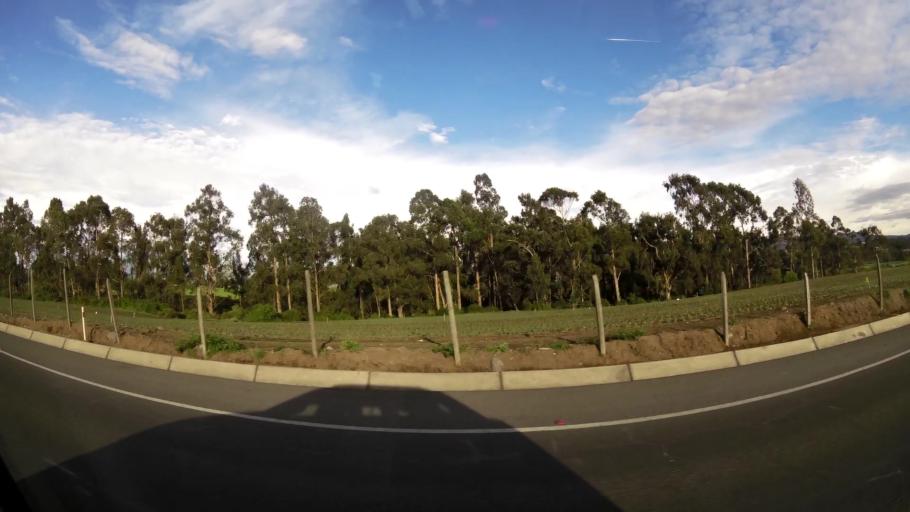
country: EC
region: Cotopaxi
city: Saquisili
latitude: -0.8412
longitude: -78.6192
